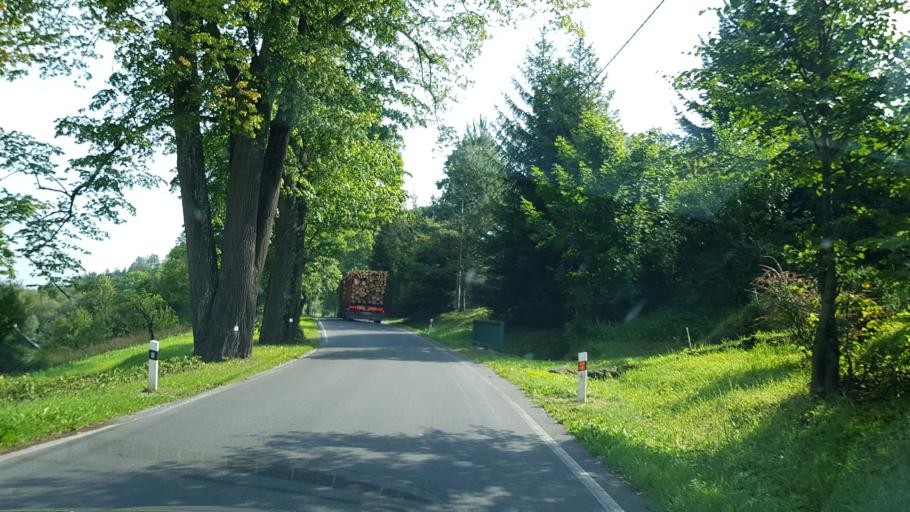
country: CZ
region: Olomoucky
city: Zlate Hory
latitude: 50.2421
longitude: 17.3498
